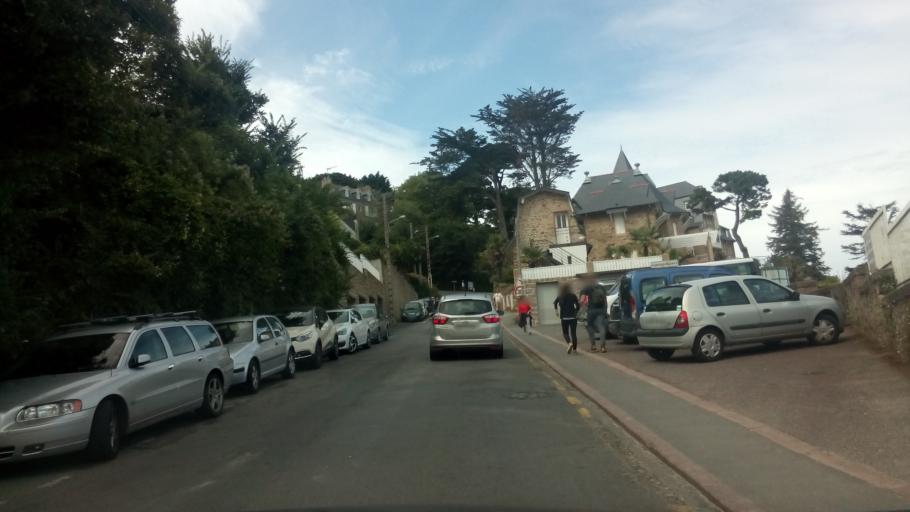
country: FR
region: Brittany
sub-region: Departement des Cotes-d'Armor
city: Perros-Guirec
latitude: 48.8176
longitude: -3.4610
